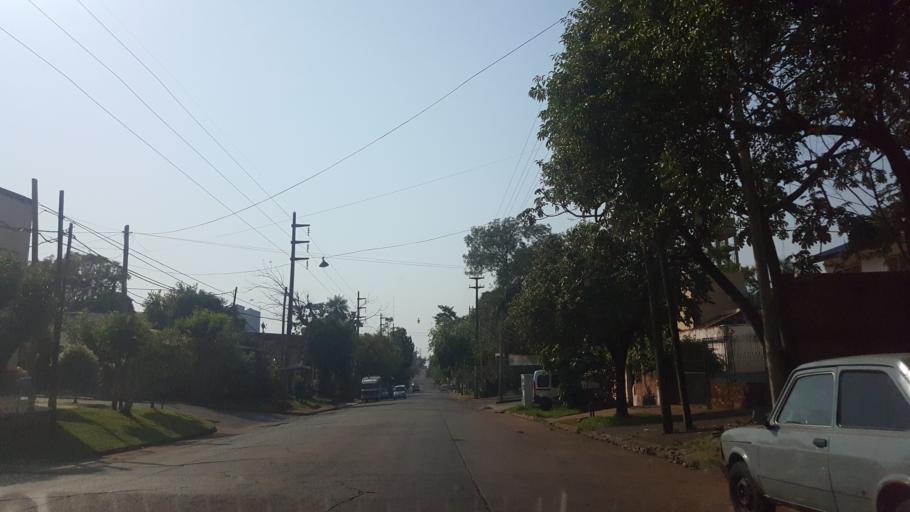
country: AR
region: Misiones
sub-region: Departamento de Capital
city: Posadas
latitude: -27.3769
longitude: -55.9053
